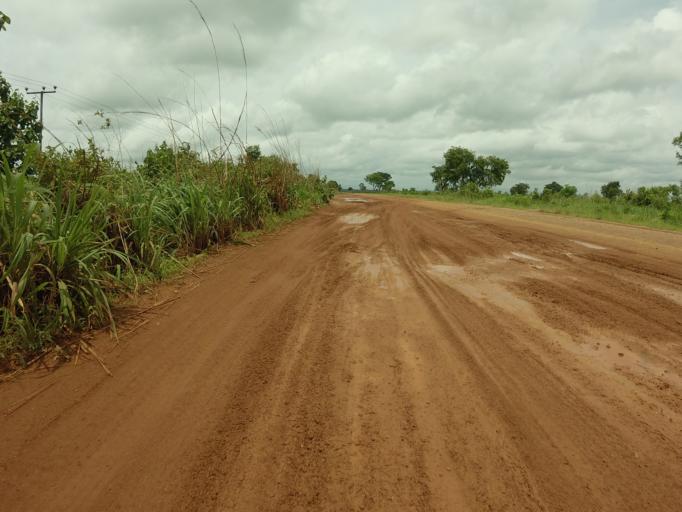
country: GH
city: Kpandae
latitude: 8.4478
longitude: 0.3517
